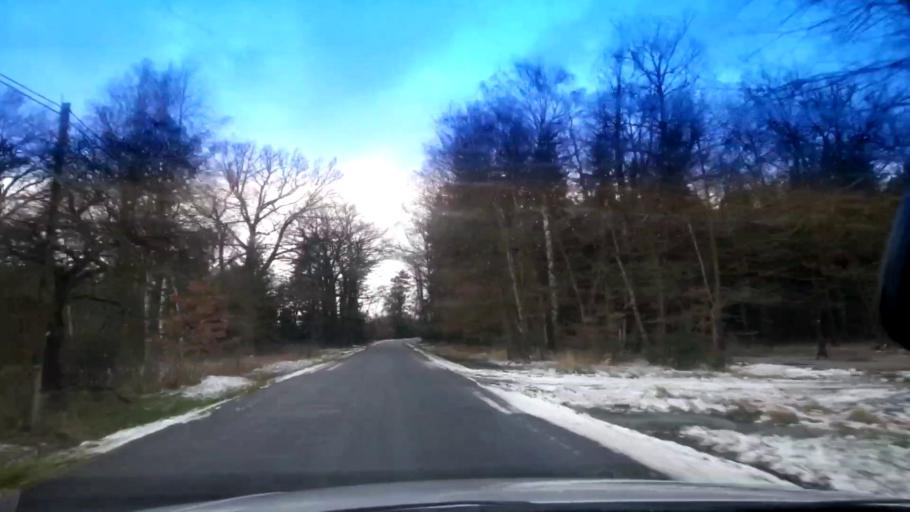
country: CZ
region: Karlovarsky
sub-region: Okres Cheb
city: Cheb
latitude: 50.0427
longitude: 12.3602
